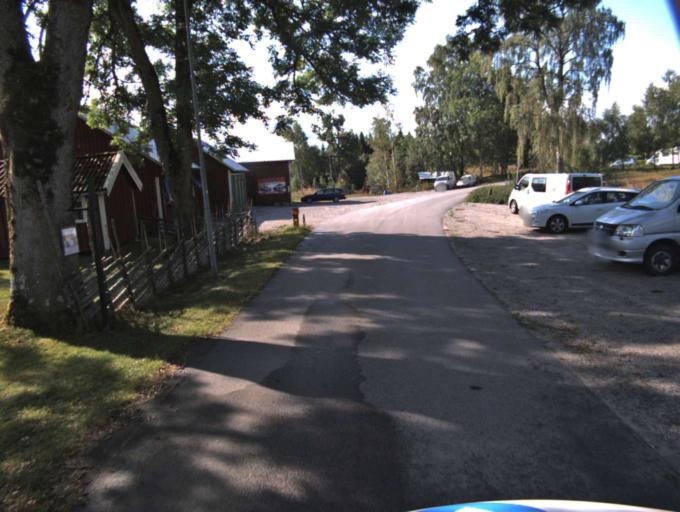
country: SE
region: Vaestra Goetaland
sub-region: Ulricehamns Kommun
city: Ulricehamn
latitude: 57.6756
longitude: 13.4720
